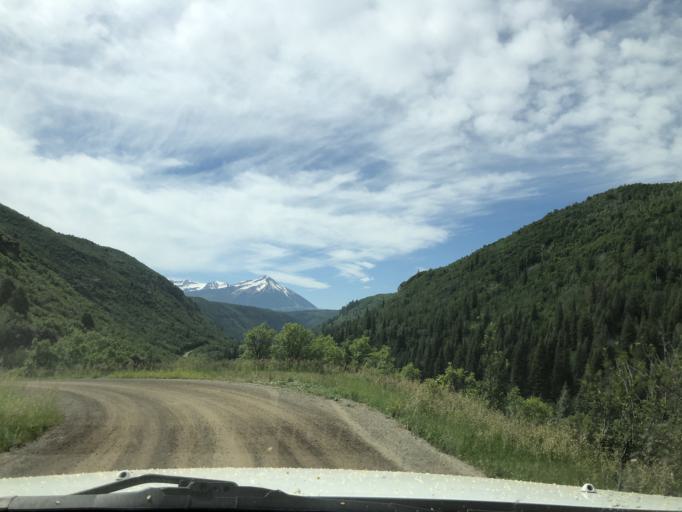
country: US
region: Colorado
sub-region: Delta County
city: Paonia
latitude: 38.9941
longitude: -107.3518
